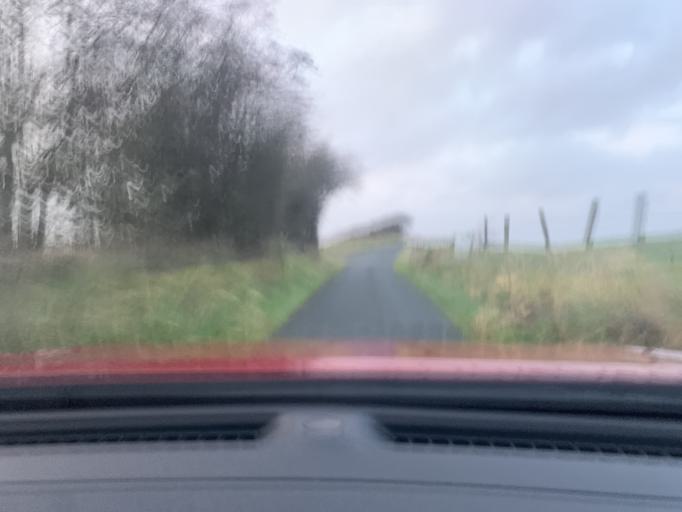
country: IE
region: Connaught
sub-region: Sligo
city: Ballymote
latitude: 54.0645
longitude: -8.3993
